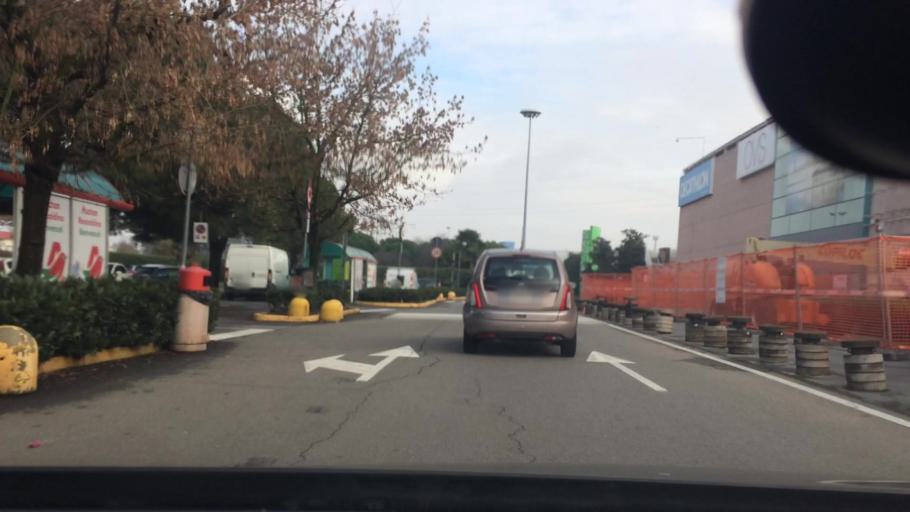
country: IT
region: Lombardy
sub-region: Citta metropolitana di Milano
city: Rescaldina
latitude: 45.6100
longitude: 8.9625
